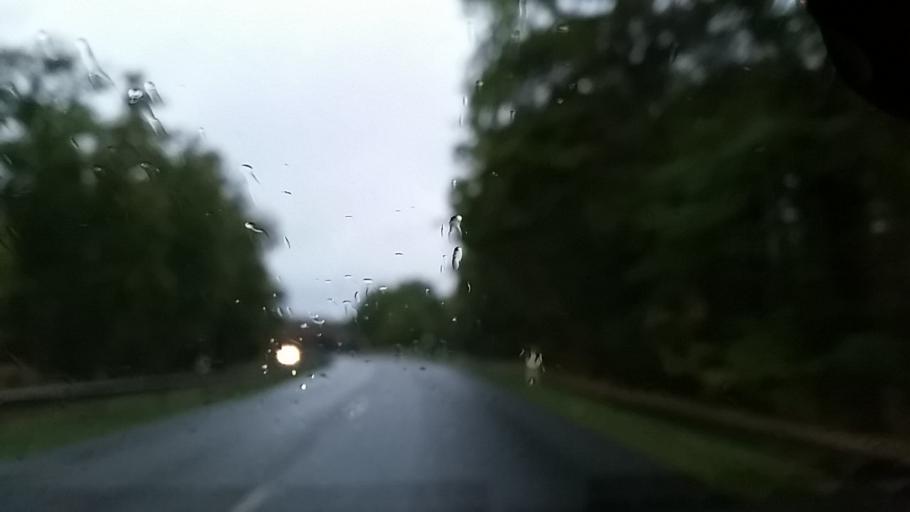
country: DE
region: Lower Saxony
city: Weyhausen
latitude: 52.4517
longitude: 10.7124
